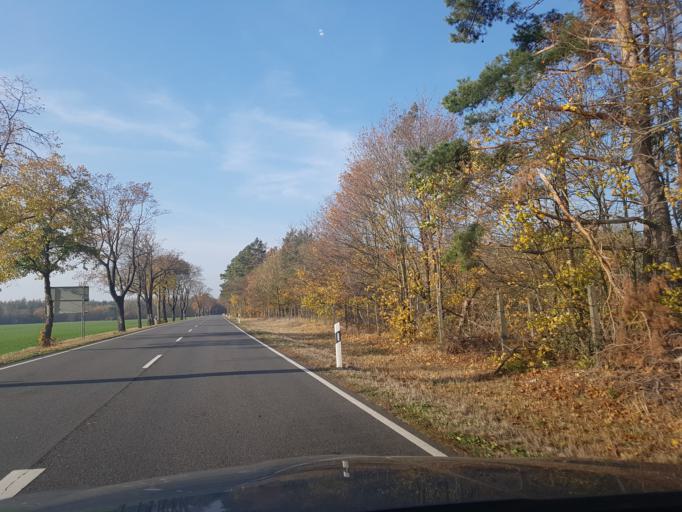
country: DE
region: Brandenburg
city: Falkenberg
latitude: 51.5421
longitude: 13.2235
